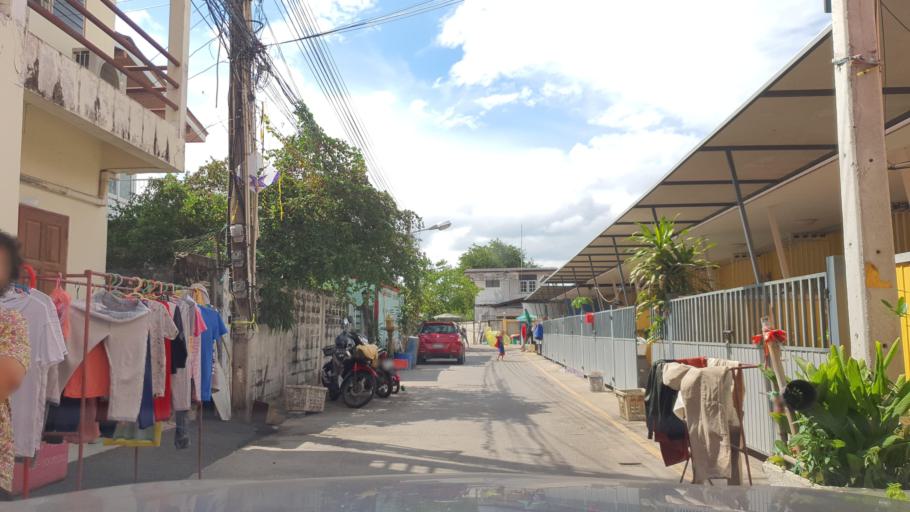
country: TH
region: Chon Buri
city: Chon Buri
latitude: 13.3699
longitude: 100.9822
